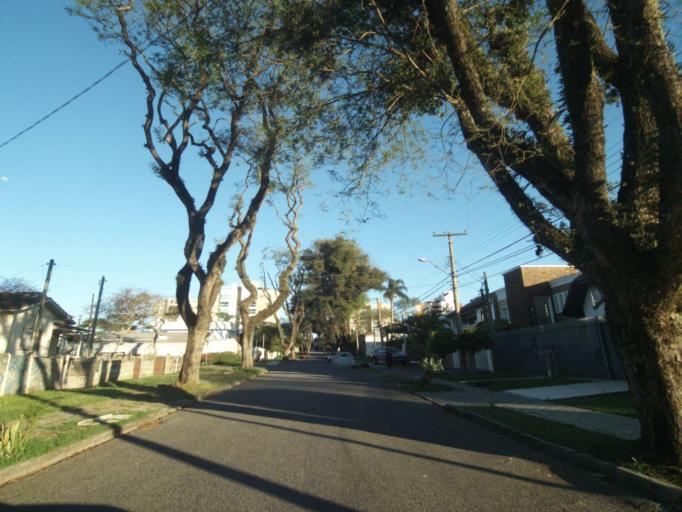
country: BR
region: Parana
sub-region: Curitiba
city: Curitiba
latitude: -25.3926
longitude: -49.2456
